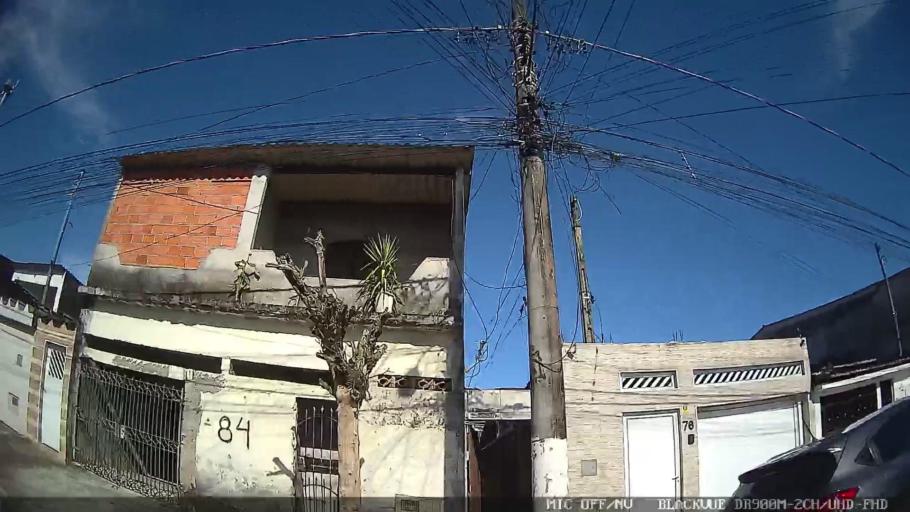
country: BR
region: Sao Paulo
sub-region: Santos
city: Santos
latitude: -23.9372
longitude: -46.2839
